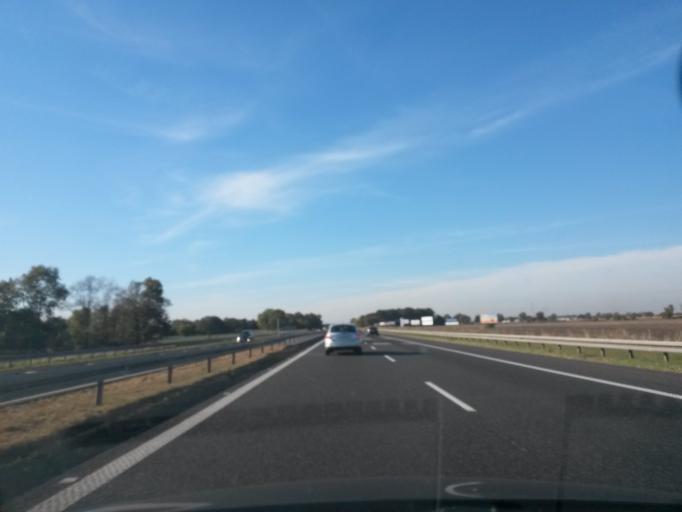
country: PL
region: Lower Silesian Voivodeship
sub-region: Powiat wroclawski
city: Zorawina
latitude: 50.9968
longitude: 17.0448
